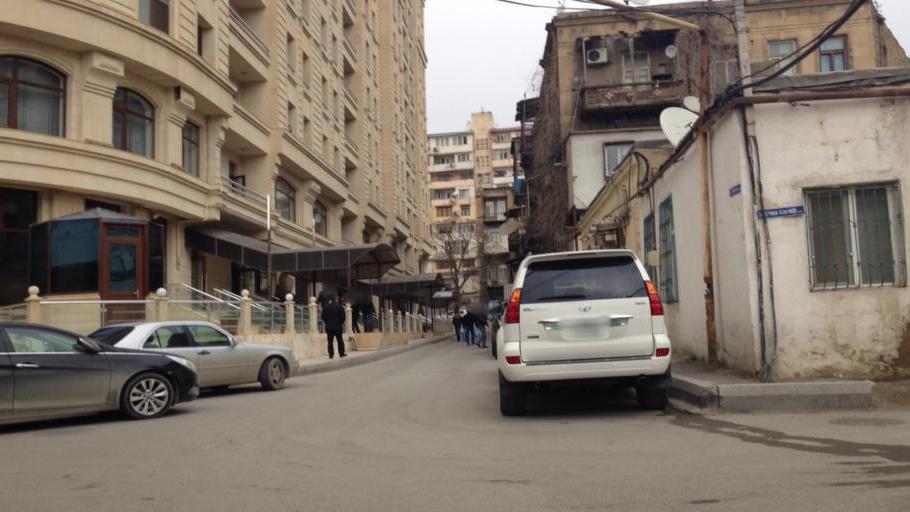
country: AZ
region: Baki
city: Badamdar
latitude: 40.3771
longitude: 49.8337
